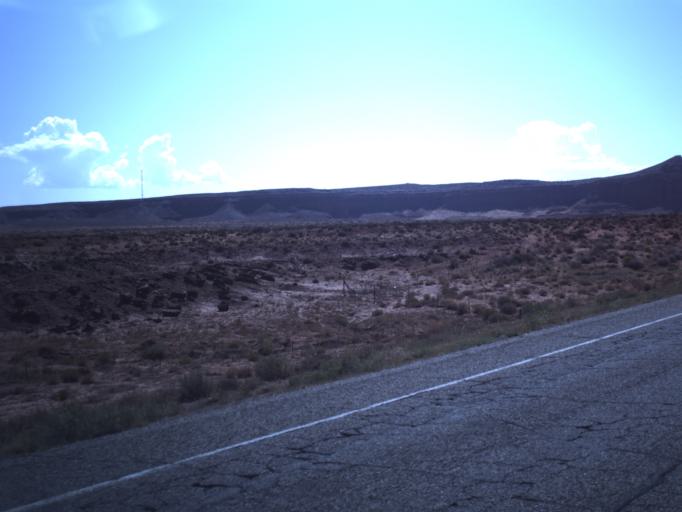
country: US
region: Utah
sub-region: San Juan County
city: Blanding
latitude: 36.9976
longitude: -109.6089
